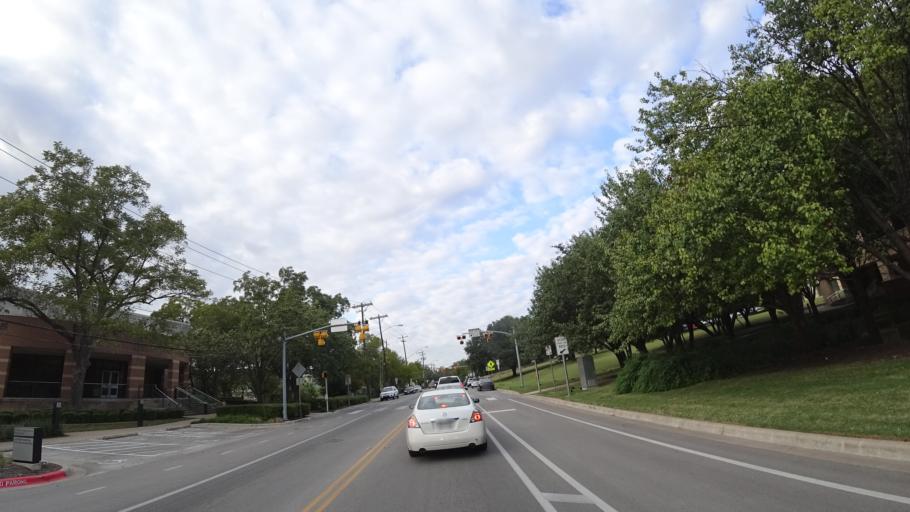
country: US
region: Texas
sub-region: Travis County
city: Rollingwood
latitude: 30.2940
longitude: -97.7836
